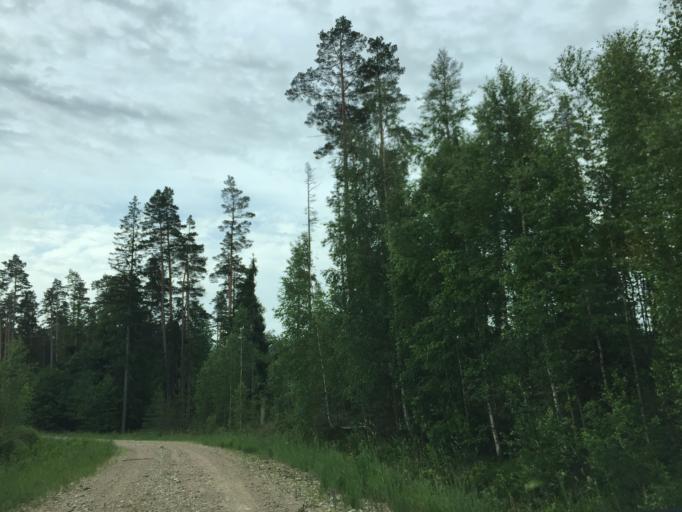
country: LV
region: Tukuma Rajons
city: Tukums
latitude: 57.0314
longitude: 23.1595
